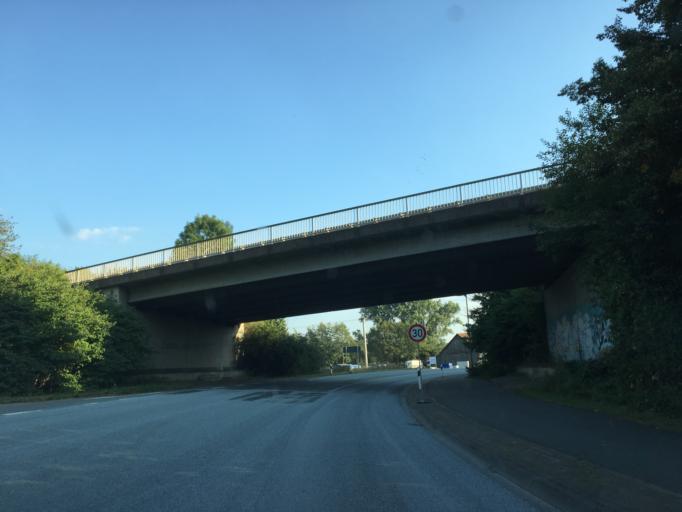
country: DE
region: Hesse
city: Frankenberg
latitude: 51.0508
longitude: 8.8022
